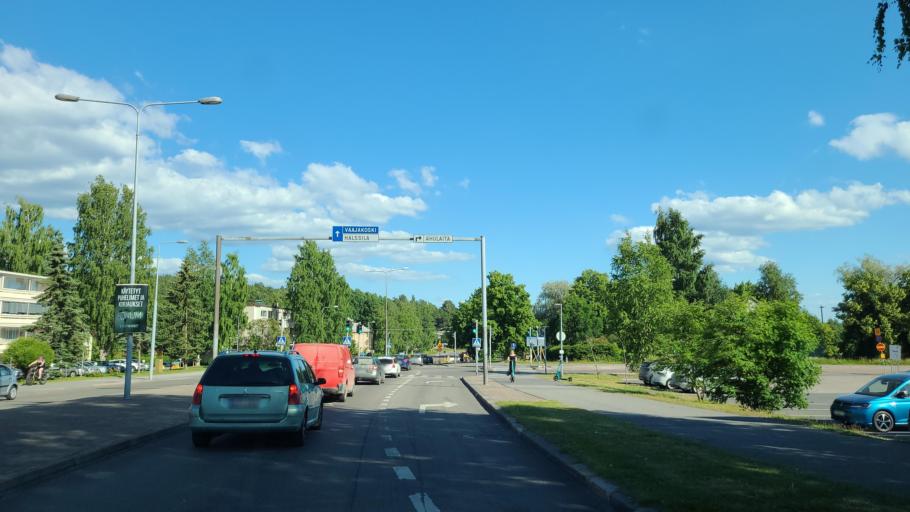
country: FI
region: Central Finland
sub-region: Jyvaeskylae
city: Jyvaeskylae
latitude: 62.2507
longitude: 25.7750
